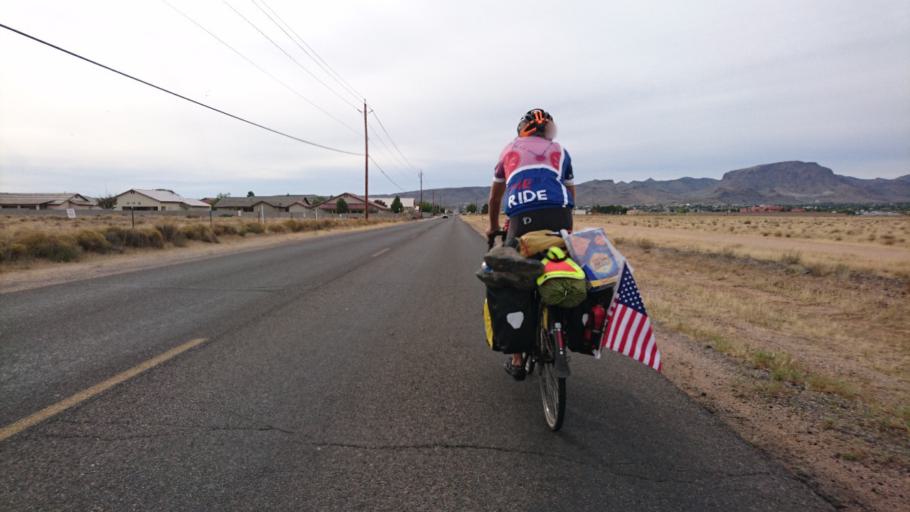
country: US
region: Arizona
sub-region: Mohave County
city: New Kingman-Butler
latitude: 35.2394
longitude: -113.9980
